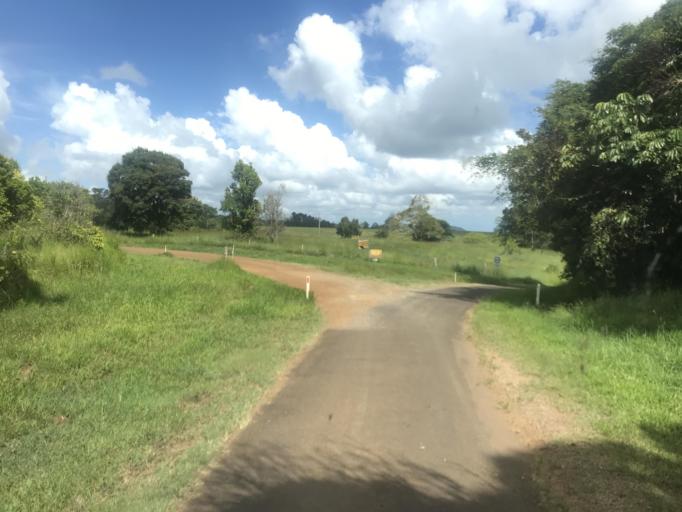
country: AU
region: Queensland
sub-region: Tablelands
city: Ravenshoe
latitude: -17.5464
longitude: 145.6970
